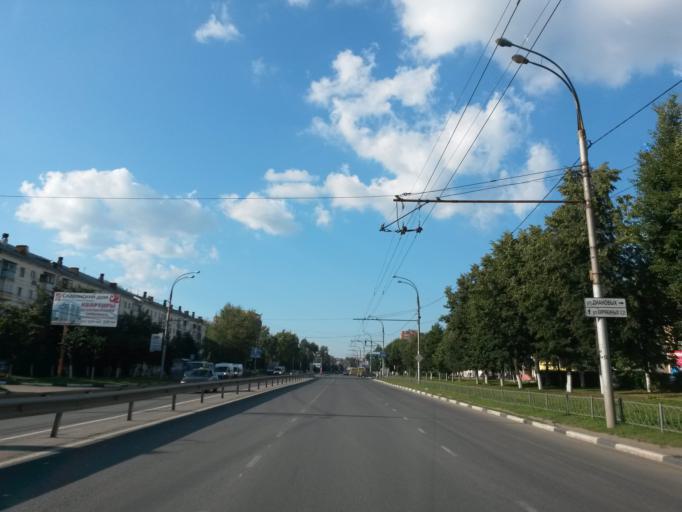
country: RU
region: Ivanovo
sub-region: Gorod Ivanovo
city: Ivanovo
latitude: 56.9660
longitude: 40.9735
